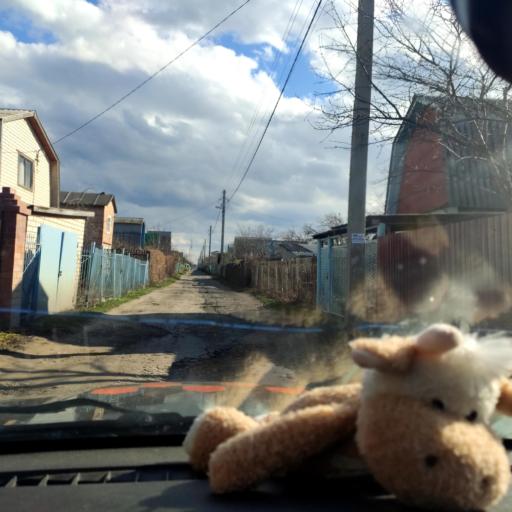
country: RU
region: Samara
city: Tol'yatti
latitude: 53.5944
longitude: 49.3087
